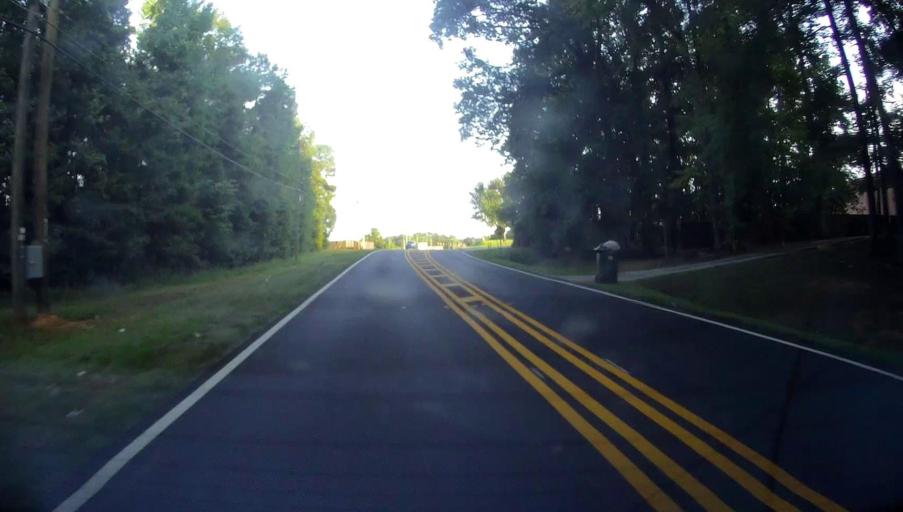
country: US
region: Georgia
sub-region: Bibb County
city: Macon
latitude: 32.9012
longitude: -83.7040
